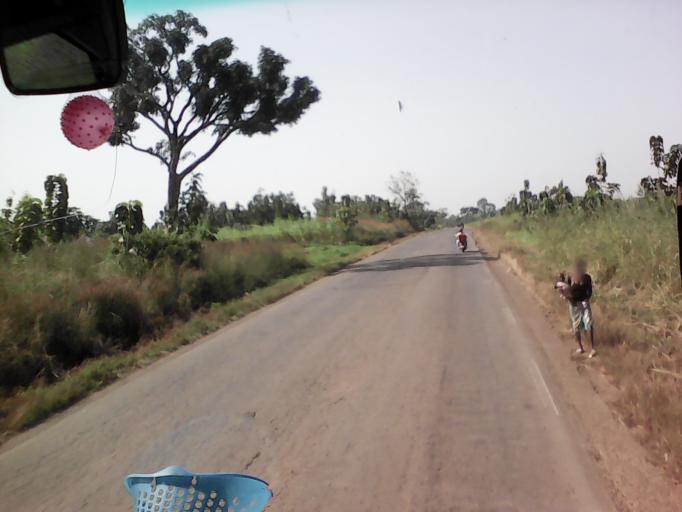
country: TG
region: Centrale
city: Sokode
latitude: 8.8752
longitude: 1.0815
